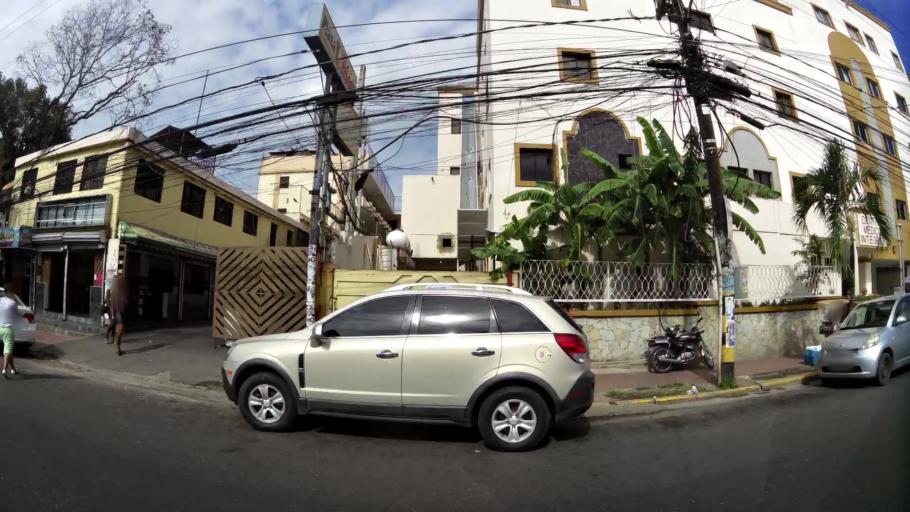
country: DO
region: Santo Domingo
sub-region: Santo Domingo
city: Santo Domingo Este
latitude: 18.4877
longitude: -69.8656
